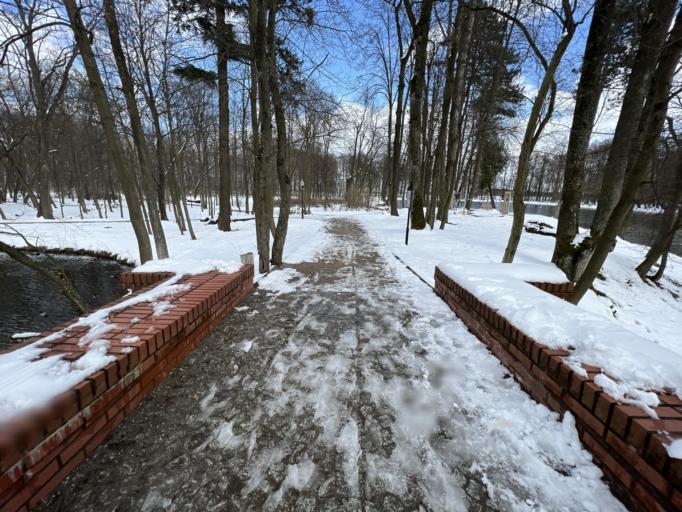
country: PL
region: Masovian Voivodeship
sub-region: Powiat pruszkowski
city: Nadarzyn
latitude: 52.0450
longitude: 20.7807
